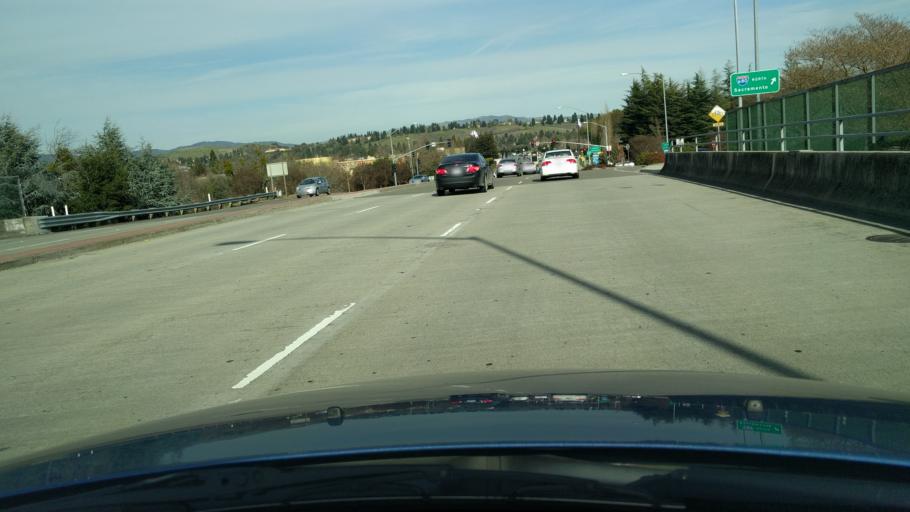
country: US
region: California
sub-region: Contra Costa County
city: San Ramon
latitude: 37.7600
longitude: -121.9653
